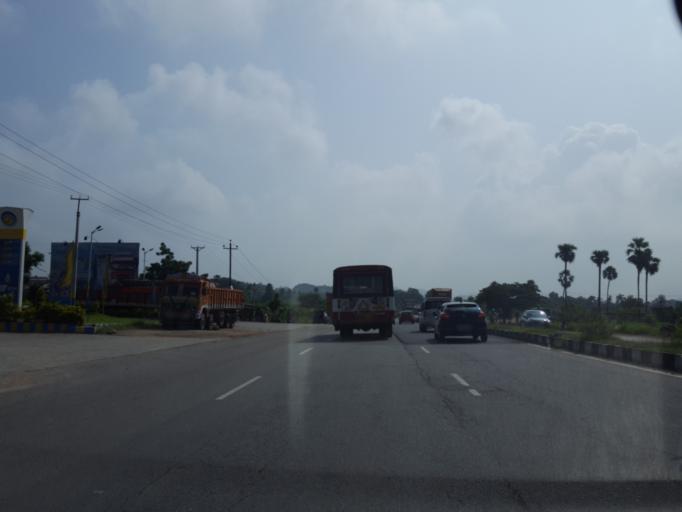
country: IN
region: Telangana
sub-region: Rangareddi
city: Ghatkesar
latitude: 17.3065
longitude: 78.7234
